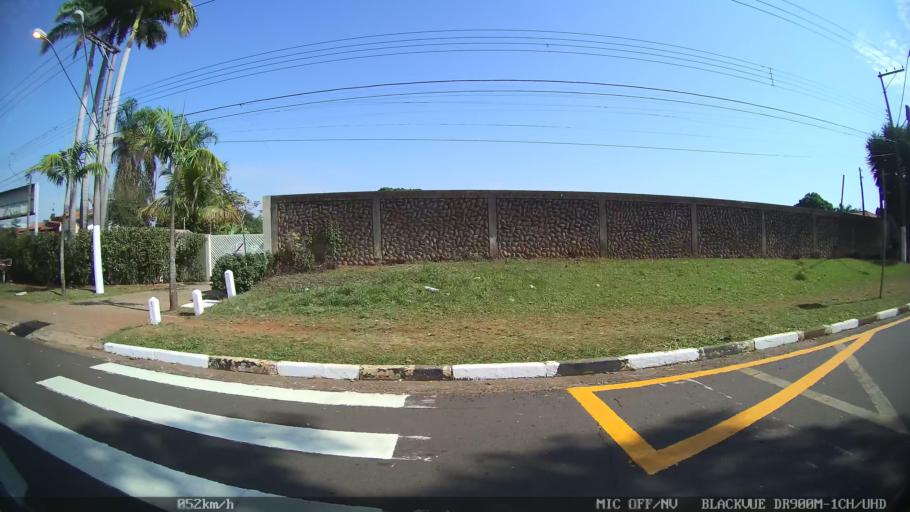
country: BR
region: Sao Paulo
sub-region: Paulinia
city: Paulinia
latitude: -22.7861
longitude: -47.1405
